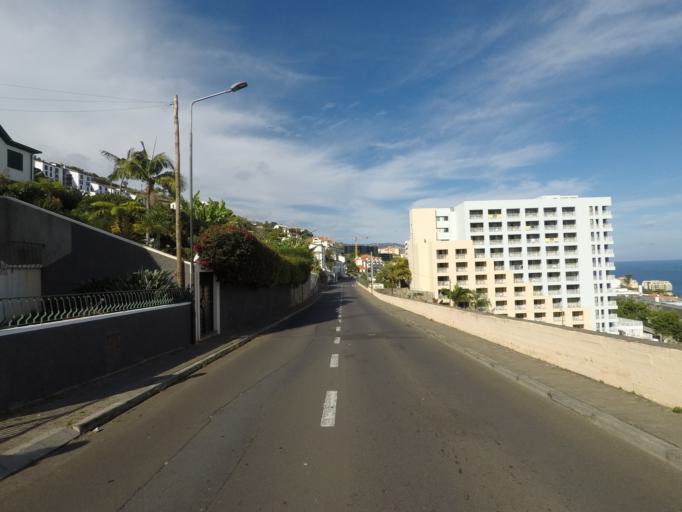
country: PT
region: Madeira
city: Camara de Lobos
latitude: 32.6384
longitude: -16.9378
